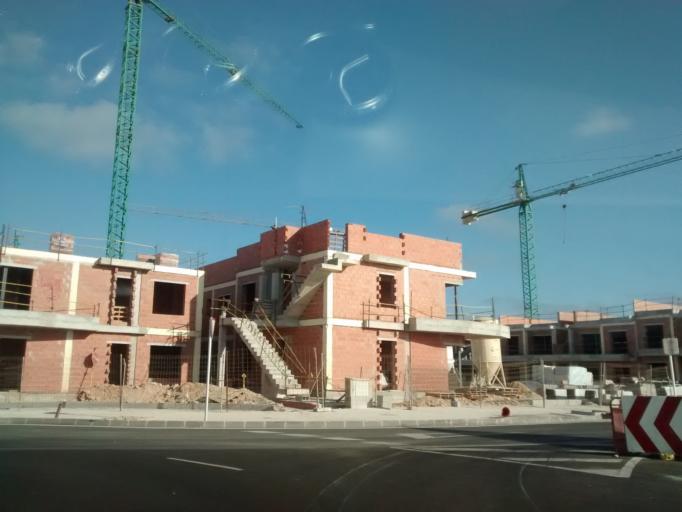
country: ES
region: Valencia
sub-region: Provincia de Alicante
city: Pilar de la Horadada
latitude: 37.8814
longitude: -0.7597
